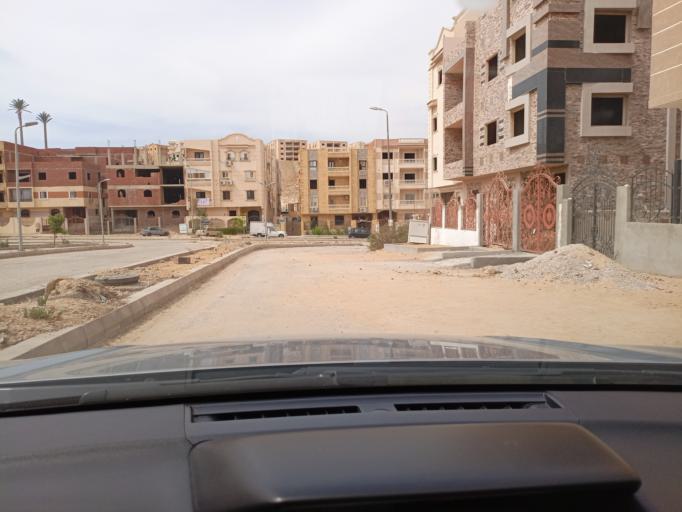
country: EG
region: Muhafazat al Qalyubiyah
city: Al Khankah
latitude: 30.2439
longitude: 31.4911
